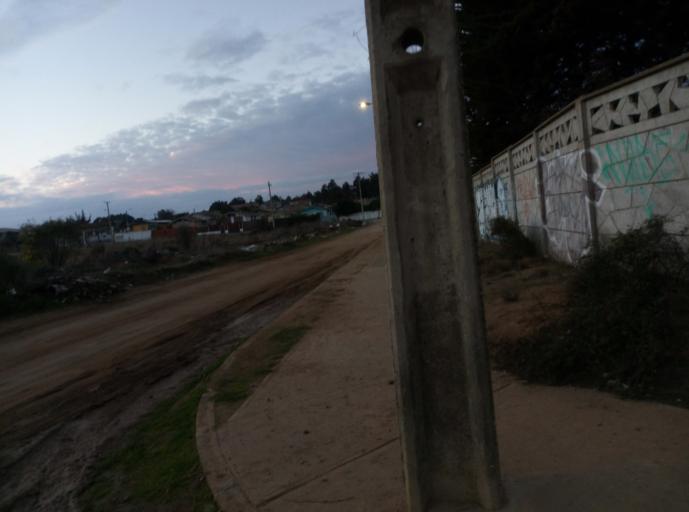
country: CL
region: Valparaiso
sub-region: San Antonio Province
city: El Tabo
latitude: -33.4236
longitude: -71.6902
